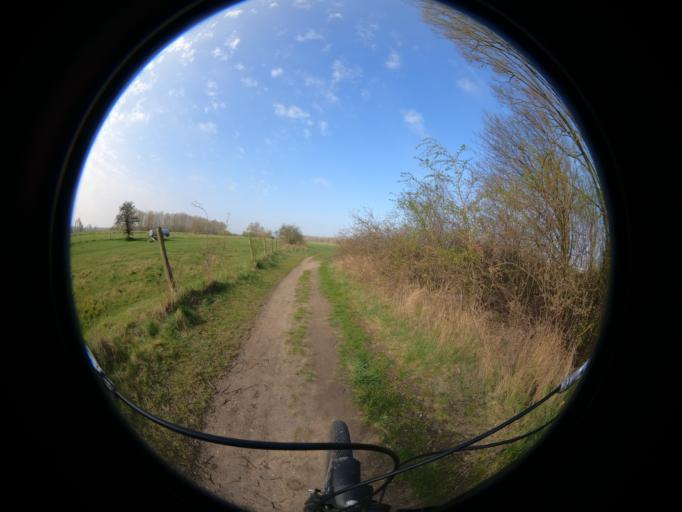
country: DE
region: Lower Saxony
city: Neu Wulmstorf
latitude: 53.5273
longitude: 9.8409
